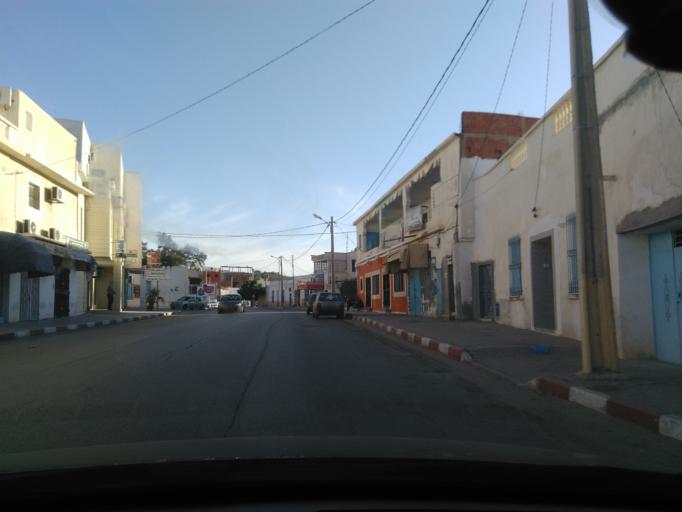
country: TN
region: Tataouine
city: Tataouine
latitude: 32.9309
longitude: 10.4500
